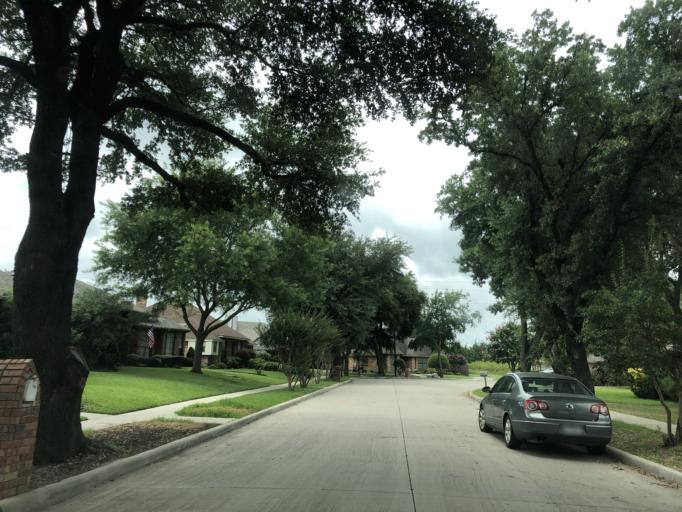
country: US
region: Texas
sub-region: Dallas County
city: Sunnyvale
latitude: 32.8388
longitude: -96.5714
